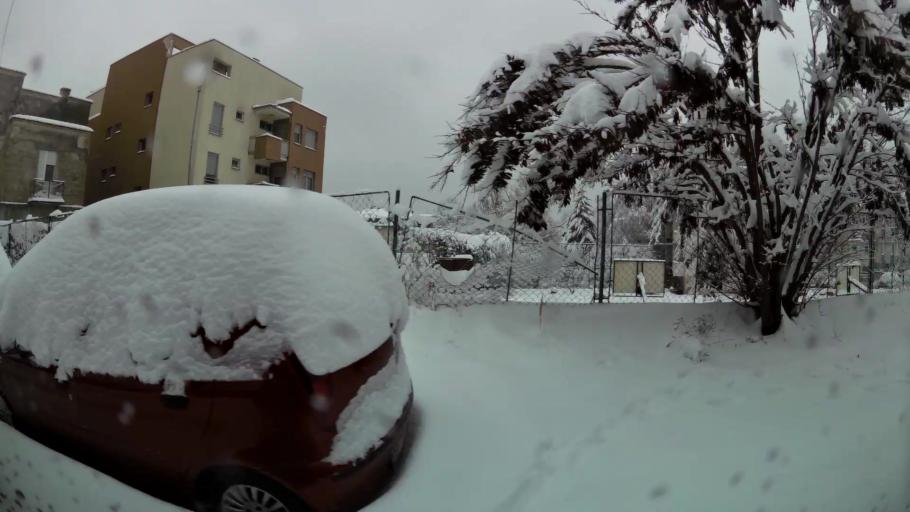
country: RS
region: Central Serbia
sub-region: Belgrade
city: Vracar
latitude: 44.7901
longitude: 20.4730
